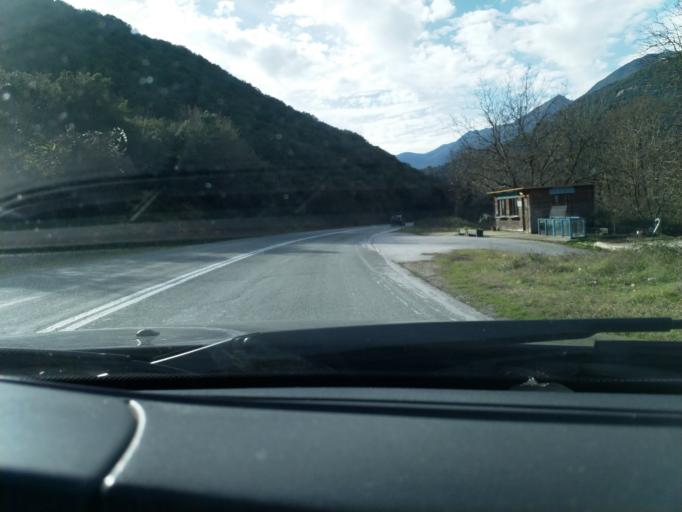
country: GR
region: Epirus
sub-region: Nomos Ioanninon
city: Agia Kyriaki
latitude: 39.4280
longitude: 20.8463
